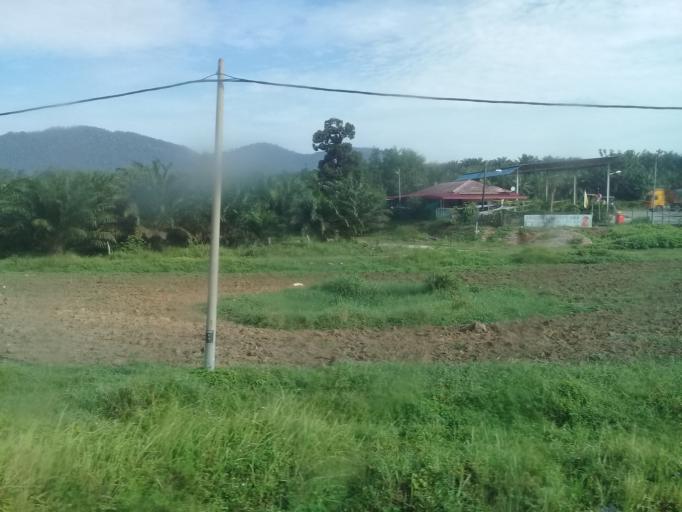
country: MY
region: Perak
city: Batu Gajah
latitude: 4.4799
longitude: 101.0027
